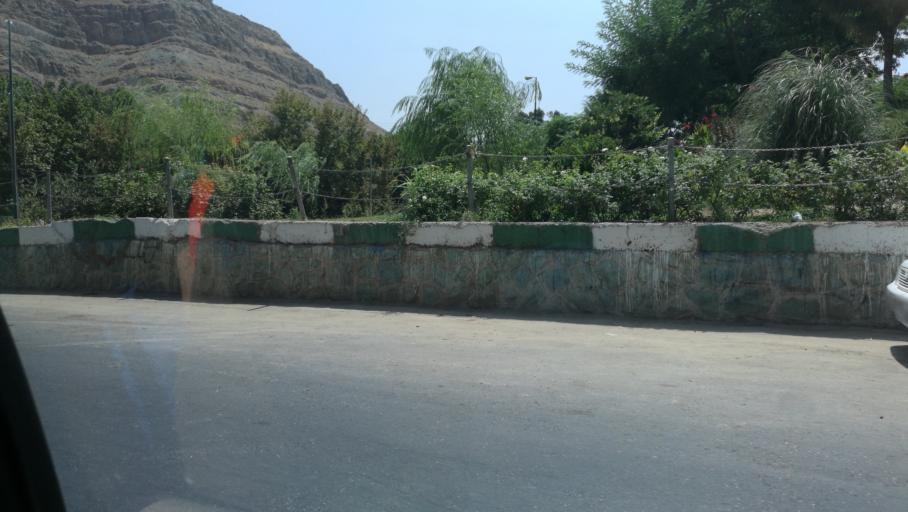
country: IR
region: Alborz
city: Karaj
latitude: 35.8356
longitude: 51.0455
